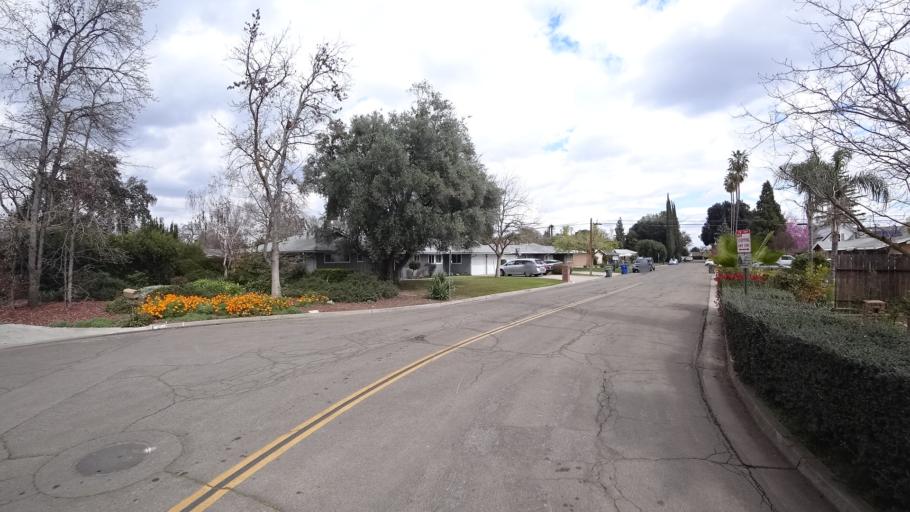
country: US
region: California
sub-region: Fresno County
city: Clovis
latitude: 36.8186
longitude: -119.7611
